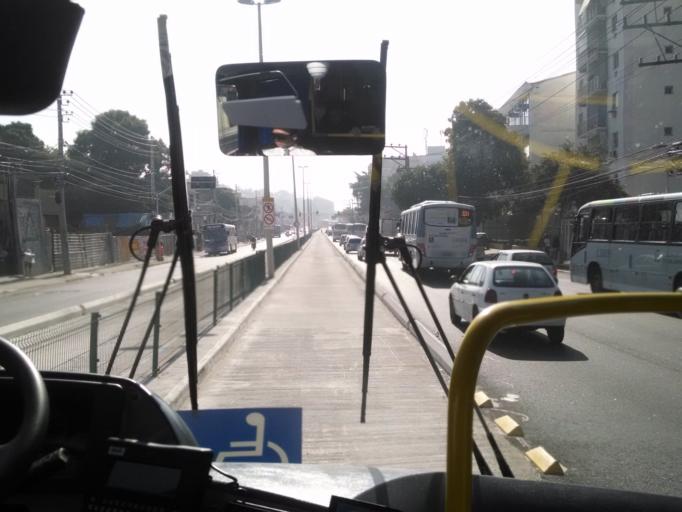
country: BR
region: Rio de Janeiro
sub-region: Sao Joao De Meriti
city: Sao Joao de Meriti
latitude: -22.9021
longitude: -43.3553
